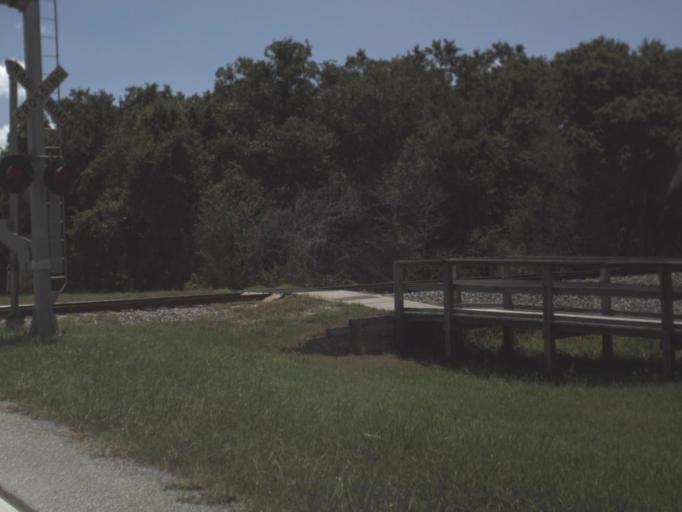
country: US
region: Florida
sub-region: Pinellas County
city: Oldsmar
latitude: 28.0252
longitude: -82.6919
